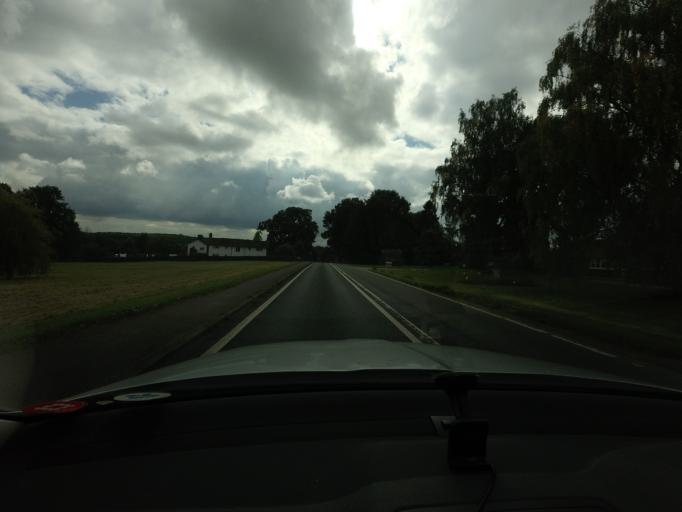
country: GB
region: England
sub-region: Kent
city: Borough Green
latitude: 51.2464
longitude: 0.2796
